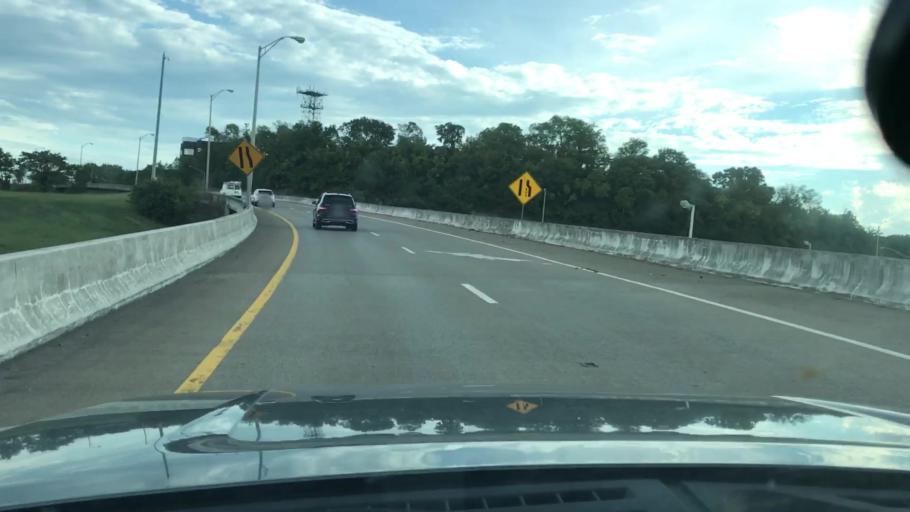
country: US
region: Tennessee
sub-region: Davidson County
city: Nashville
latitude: 36.1490
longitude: -86.7881
